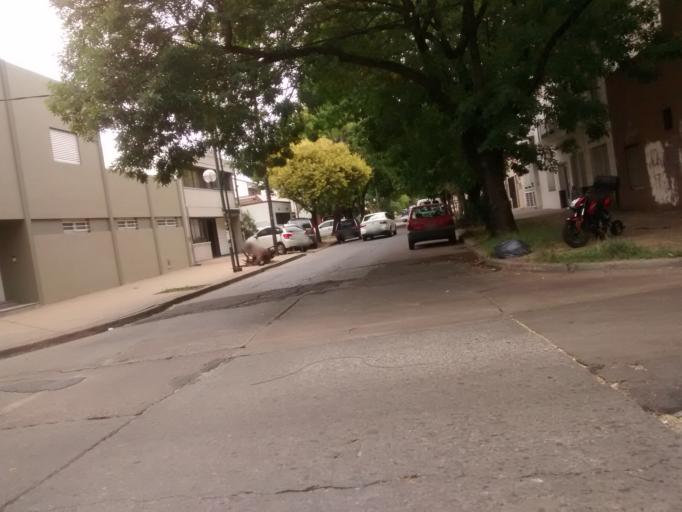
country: AR
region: Buenos Aires
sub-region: Partido de La Plata
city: La Plata
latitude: -34.9030
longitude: -57.9634
